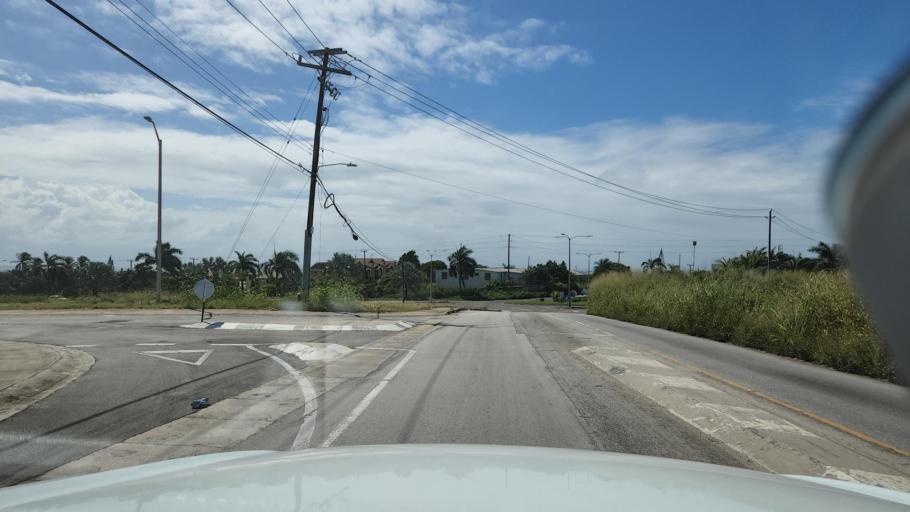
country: BB
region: Christ Church
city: Oistins
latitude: 13.0812
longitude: -59.5298
